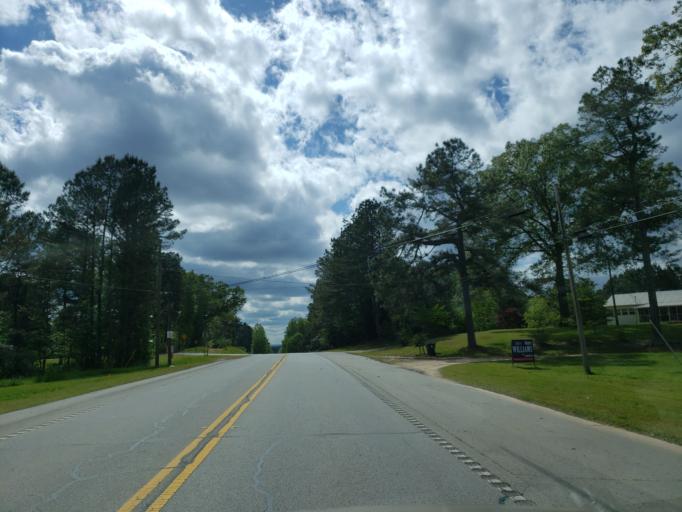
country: US
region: Georgia
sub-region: Haralson County
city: Tallapoosa
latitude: 33.7419
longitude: -85.3182
